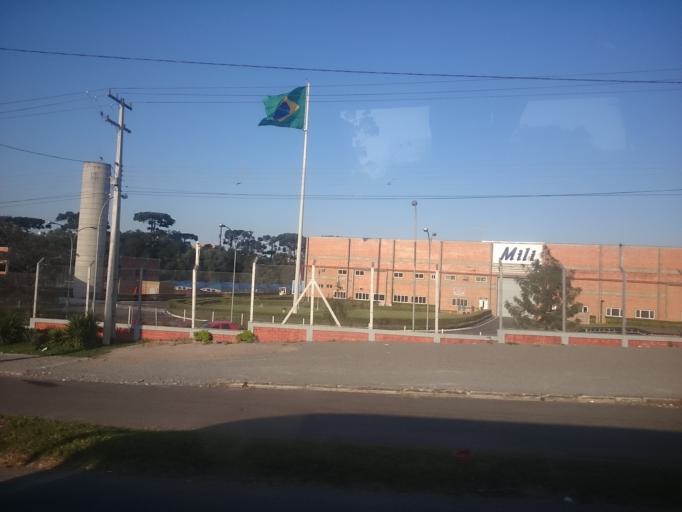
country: BR
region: Parana
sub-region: Sao Jose Dos Pinhais
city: Sao Jose dos Pinhais
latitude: -25.5409
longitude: -49.3024
